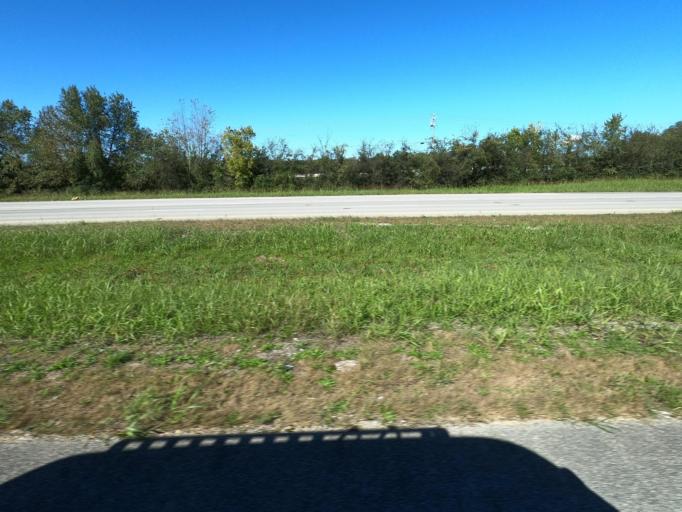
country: US
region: Tennessee
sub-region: Maury County
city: Mount Pleasant
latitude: 35.5616
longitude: -87.1797
